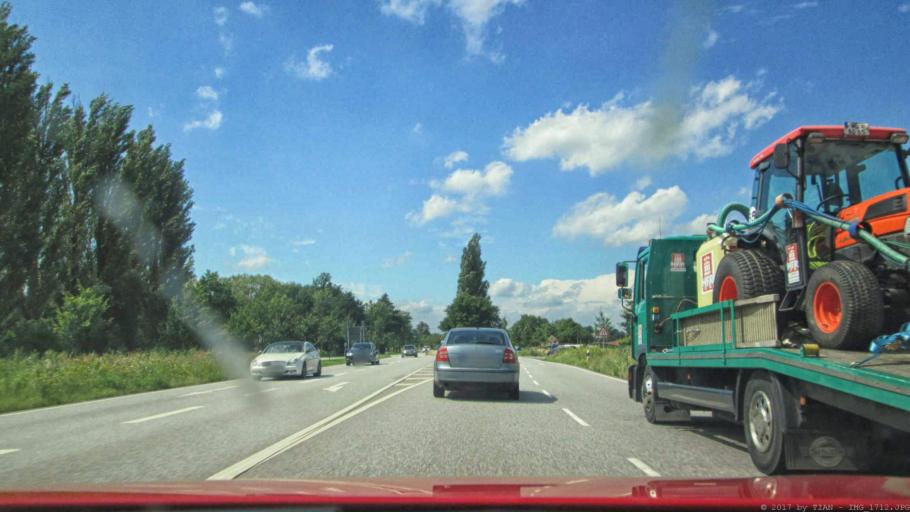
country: DE
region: Hamburg
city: Harburg
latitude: 53.4632
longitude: 10.0203
